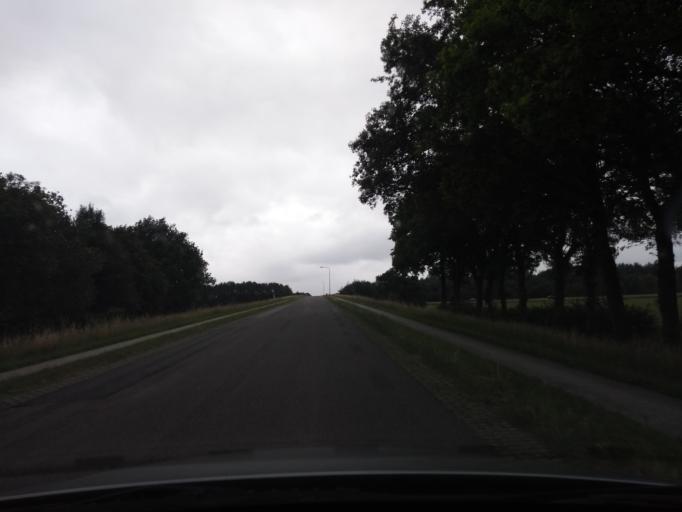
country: NL
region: Overijssel
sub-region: Gemeente Staphorst
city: Staphorst
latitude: 52.6775
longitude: 6.2994
